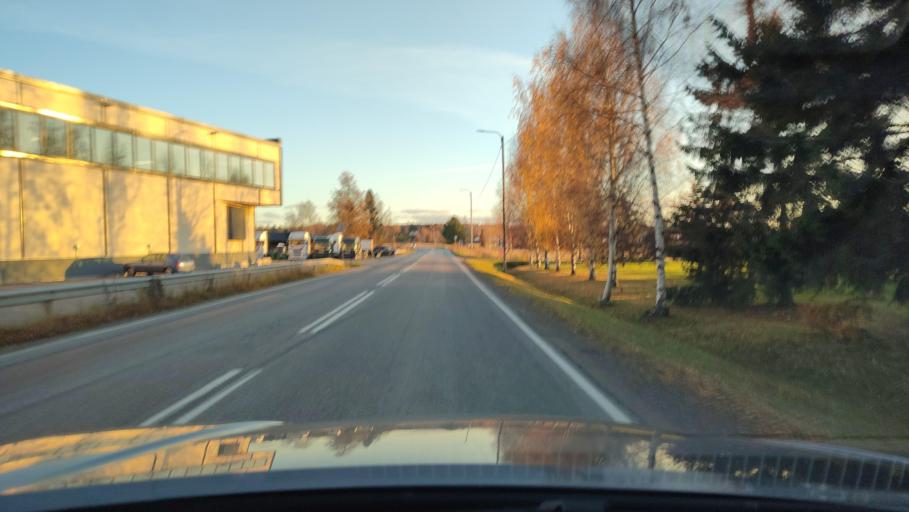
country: FI
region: Ostrobothnia
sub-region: Sydosterbotten
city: Naerpes
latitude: 62.4418
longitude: 21.3509
